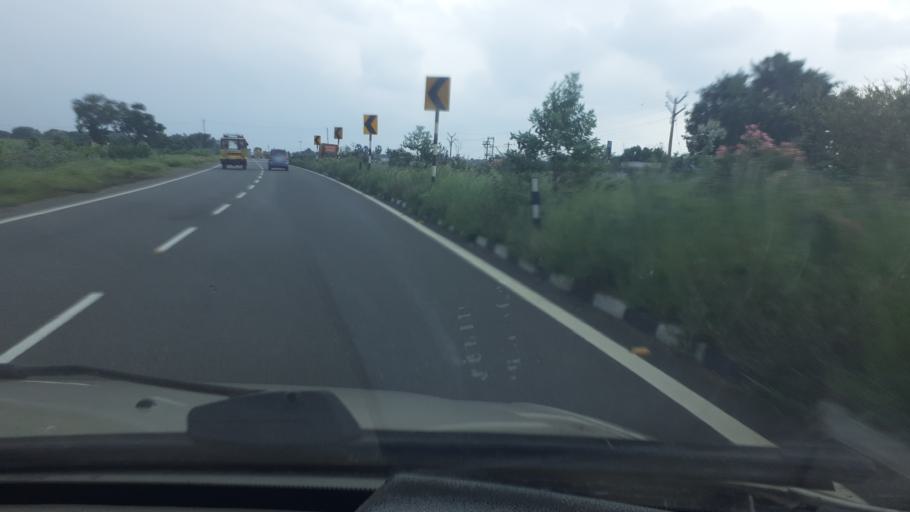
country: IN
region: Tamil Nadu
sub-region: Virudhunagar
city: Virudunagar
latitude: 9.6859
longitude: 77.9696
